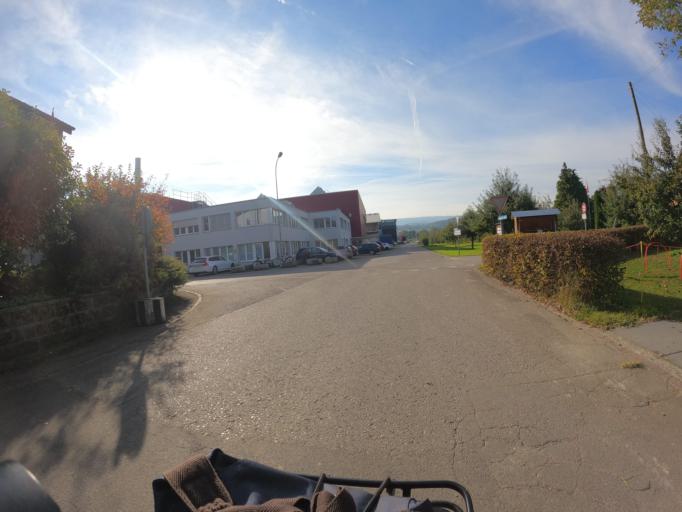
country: CH
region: Aargau
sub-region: Bezirk Muri
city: Merenschwand
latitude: 47.2622
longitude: 8.3873
